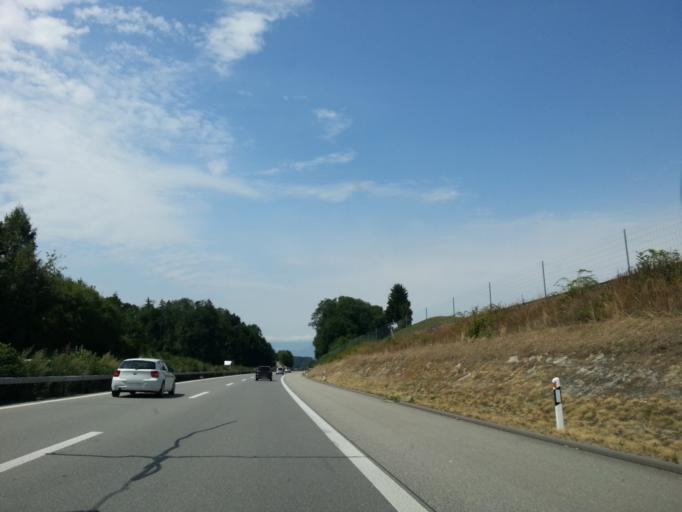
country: CH
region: Bern
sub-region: Bern-Mittelland District
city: Muhleberg
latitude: 46.9590
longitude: 7.2898
